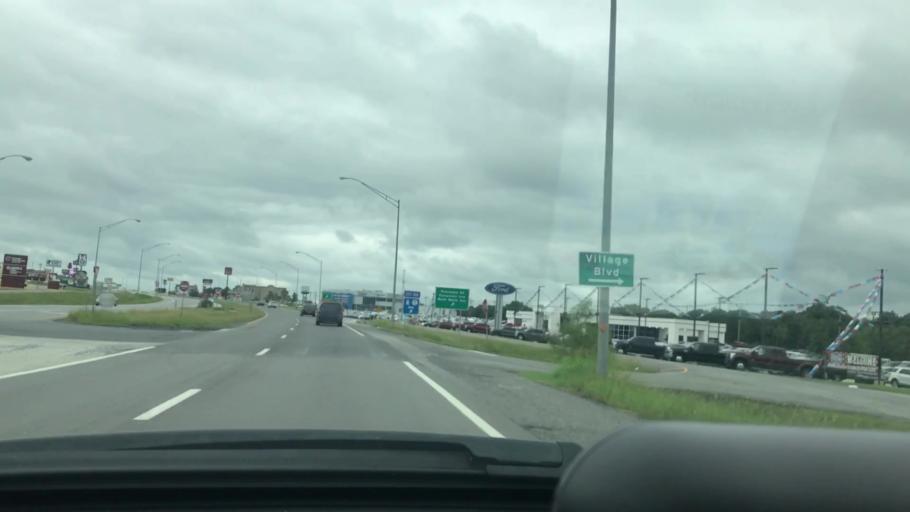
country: US
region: Oklahoma
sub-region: Pittsburg County
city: McAlester
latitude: 34.9080
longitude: -95.7458
